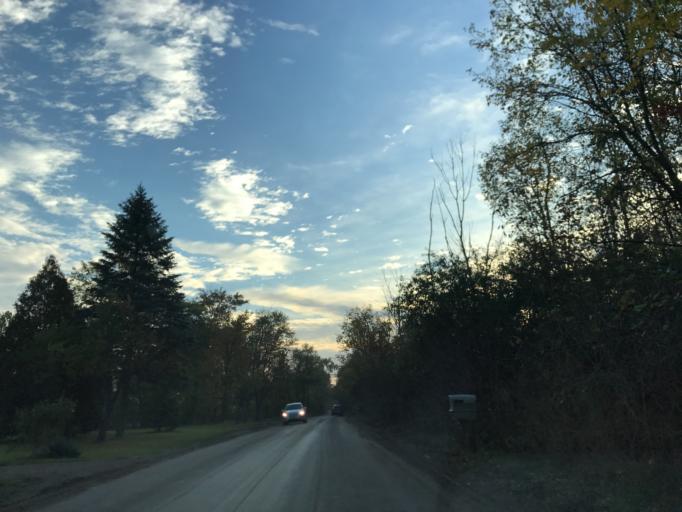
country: US
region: Michigan
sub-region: Oakland County
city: Wixom
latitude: 42.4782
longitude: -83.5620
